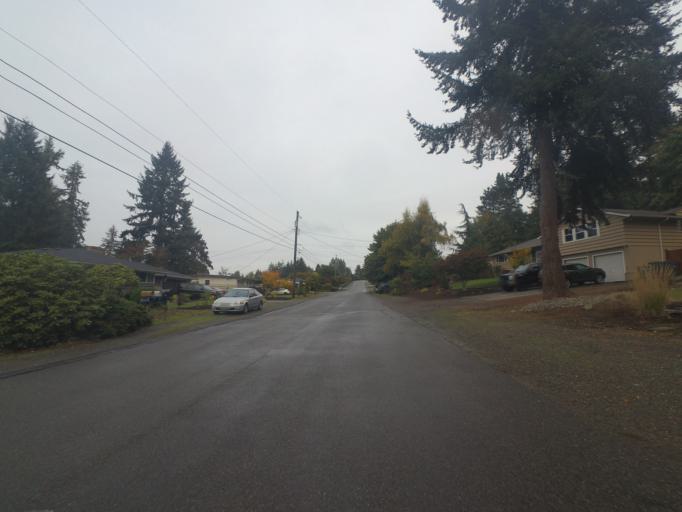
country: US
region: Washington
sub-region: Pierce County
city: University Place
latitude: 47.2171
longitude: -122.5566
